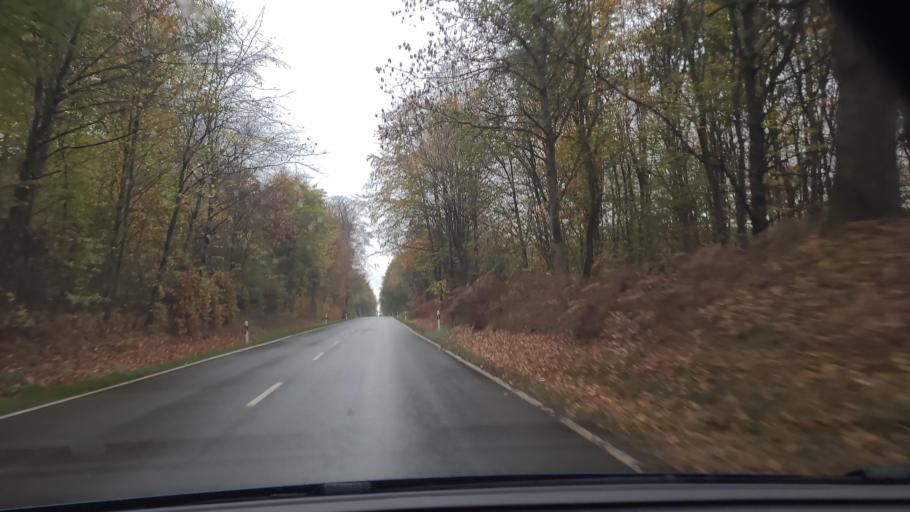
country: LU
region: Luxembourg
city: Bereldange
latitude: 49.6335
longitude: 6.1096
